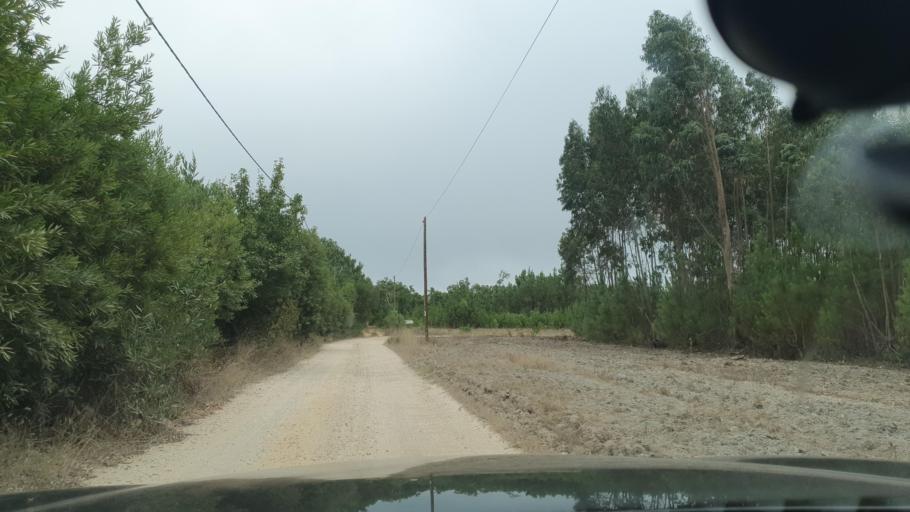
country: PT
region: Beja
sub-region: Odemira
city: Sao Teotonio
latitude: 37.4973
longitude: -8.6820
